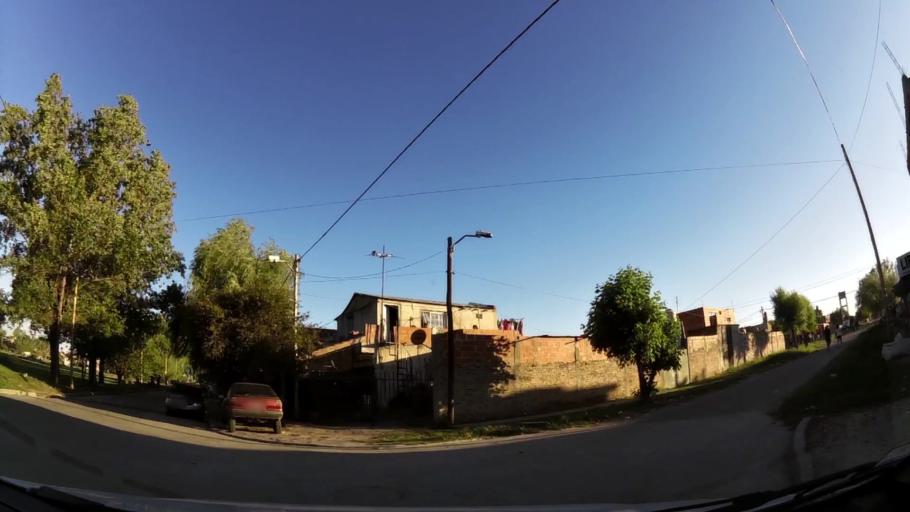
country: AR
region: Buenos Aires
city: San Justo
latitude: -34.7206
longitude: -58.6090
